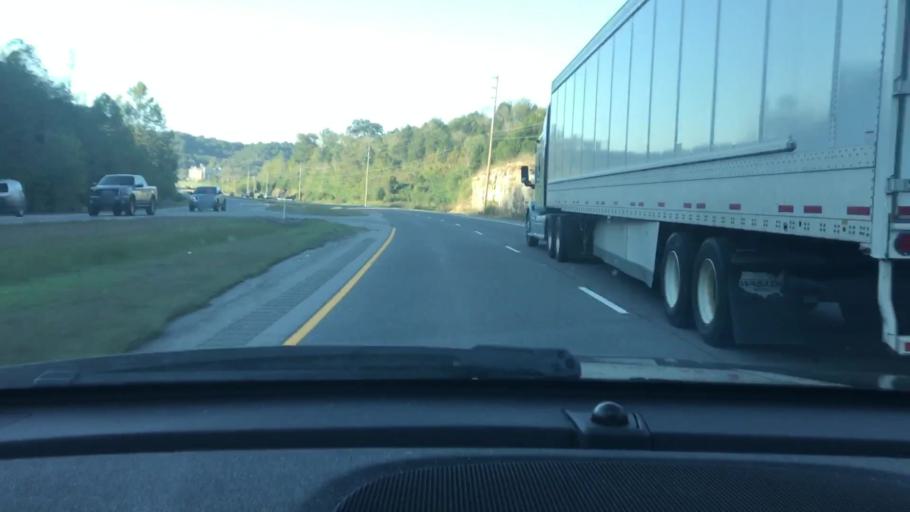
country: US
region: Tennessee
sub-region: Cheatham County
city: Ashland City
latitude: 36.2350
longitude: -87.0193
